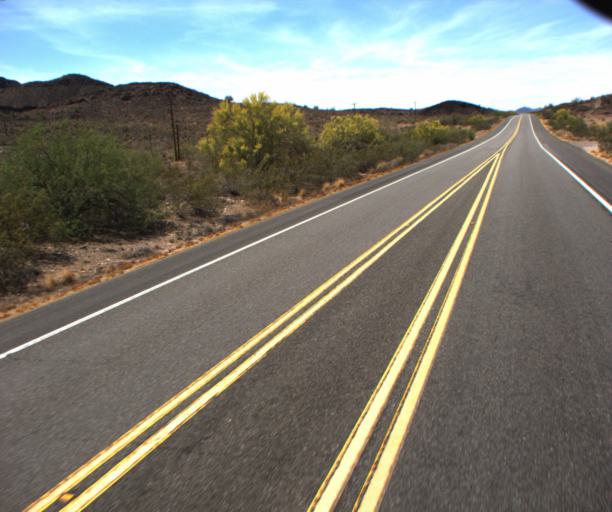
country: US
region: Arizona
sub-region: La Paz County
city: Quartzsite
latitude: 33.6849
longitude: -113.9249
